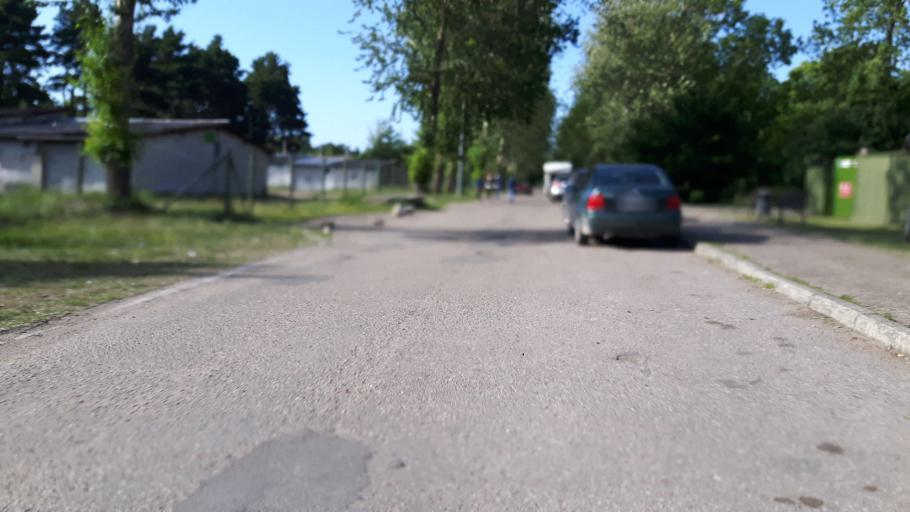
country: LV
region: Liepaja
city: Vec-Liepaja
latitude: 56.5464
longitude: 21.0203
